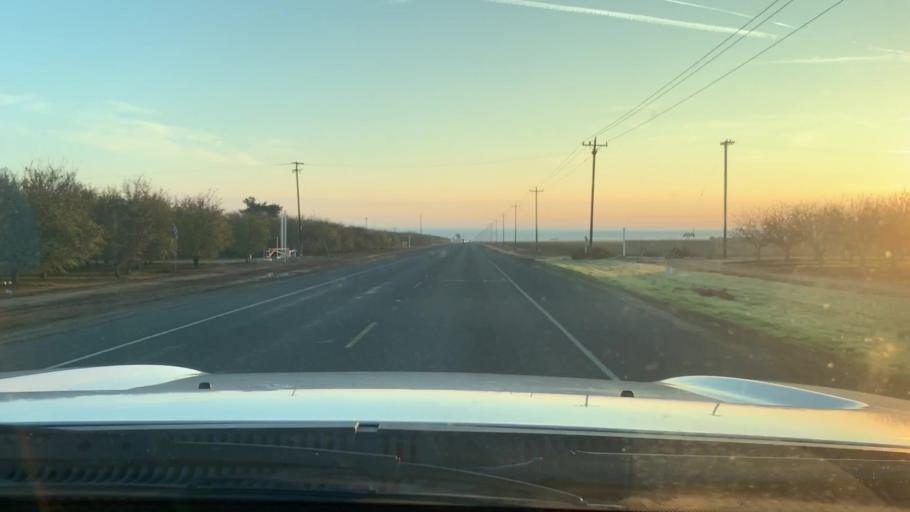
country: US
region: California
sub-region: Kern County
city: Lost Hills
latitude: 35.6012
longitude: -119.5635
